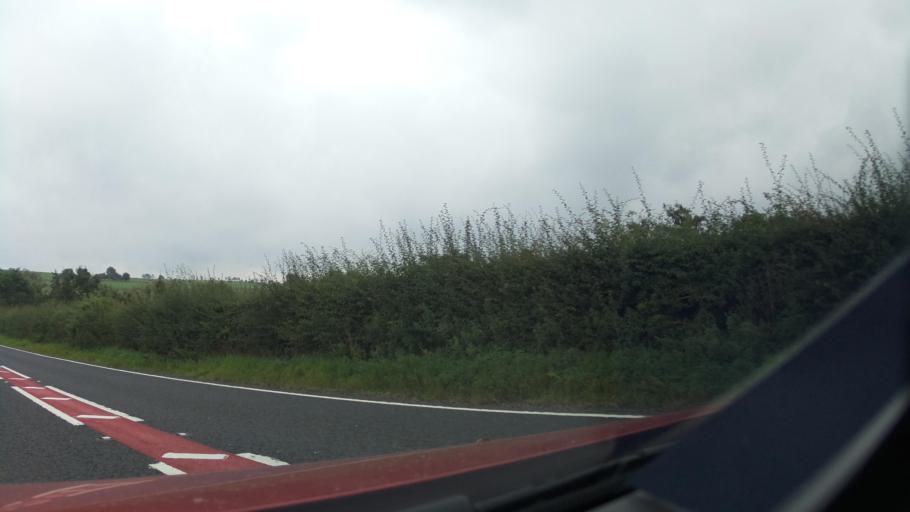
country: GB
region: England
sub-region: Northumberland
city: Rothley
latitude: 55.1556
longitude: -2.0116
